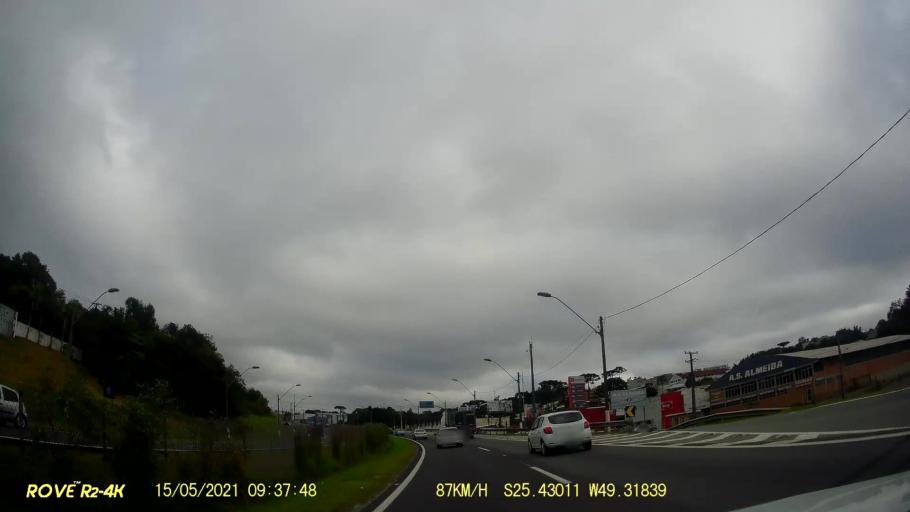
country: BR
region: Parana
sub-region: Curitiba
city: Curitiba
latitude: -25.4304
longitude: -49.3186
